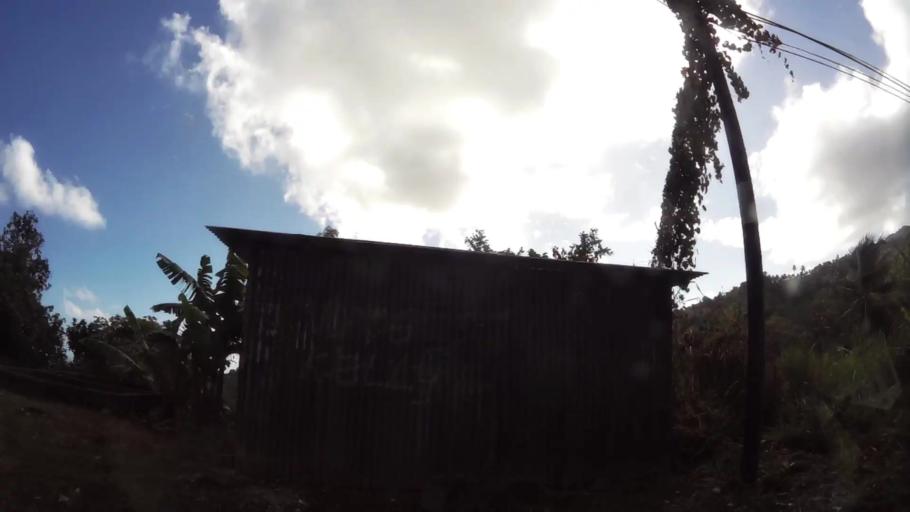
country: DM
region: Saint Andrew
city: Marigot
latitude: 15.4989
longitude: -61.2637
